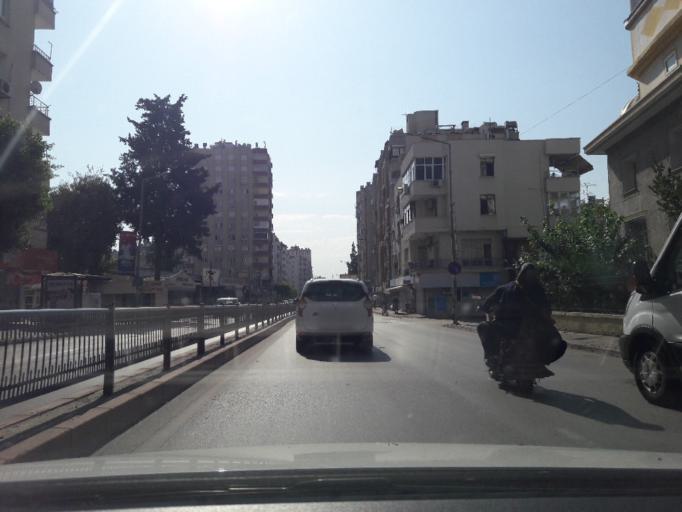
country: TR
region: Adana
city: Adana
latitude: 37.0118
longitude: 35.3230
